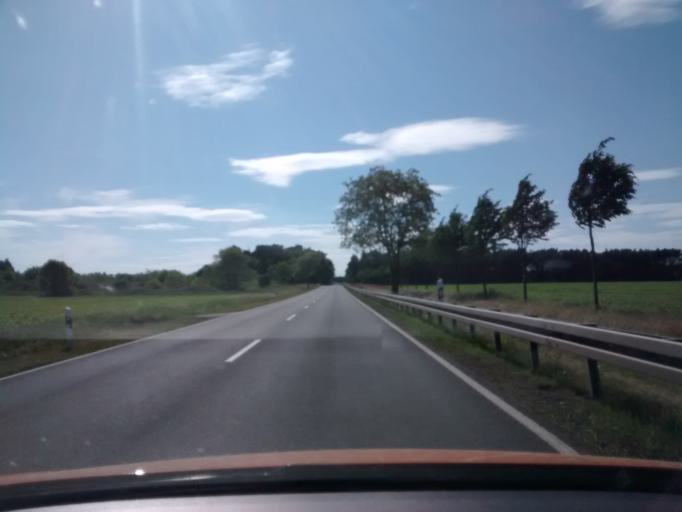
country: DE
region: Brandenburg
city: Juterbog
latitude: 51.9861
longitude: 13.1439
